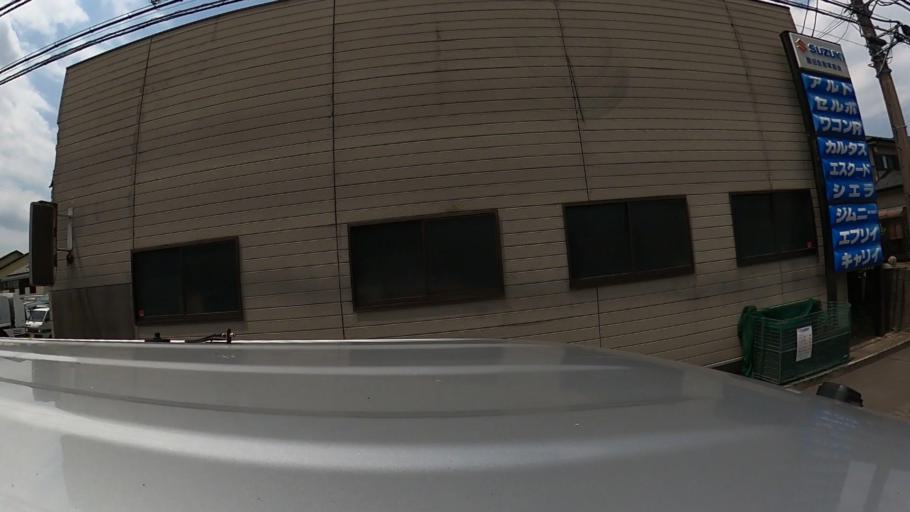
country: JP
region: Kanagawa
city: Chigasaki
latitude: 35.3792
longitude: 139.3992
